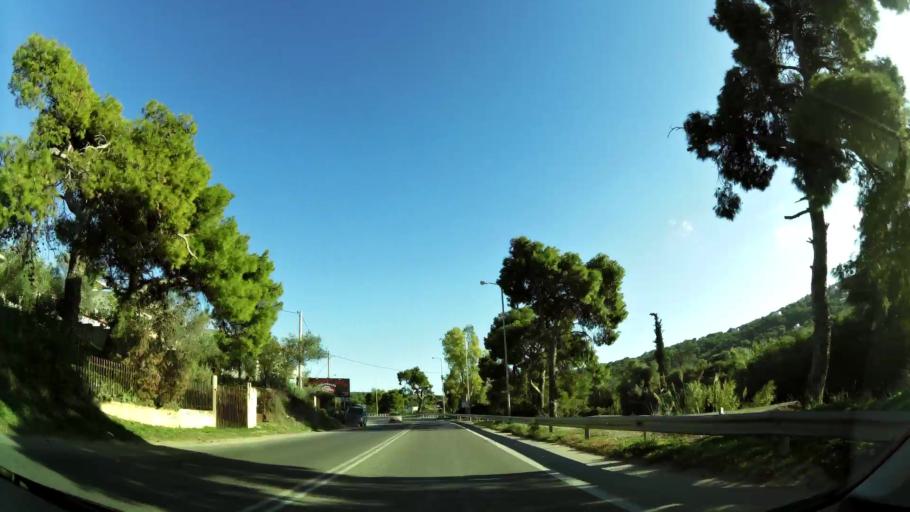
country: GR
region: Attica
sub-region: Nomarchia Anatolikis Attikis
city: Rafina
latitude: 38.0192
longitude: 23.9948
